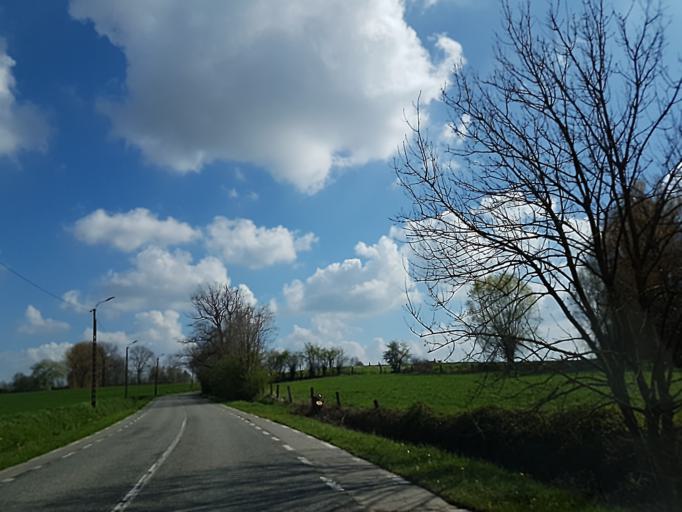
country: BE
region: Flanders
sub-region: Provincie Oost-Vlaanderen
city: Sint-Maria-Lierde
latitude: 50.8297
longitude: 3.8759
